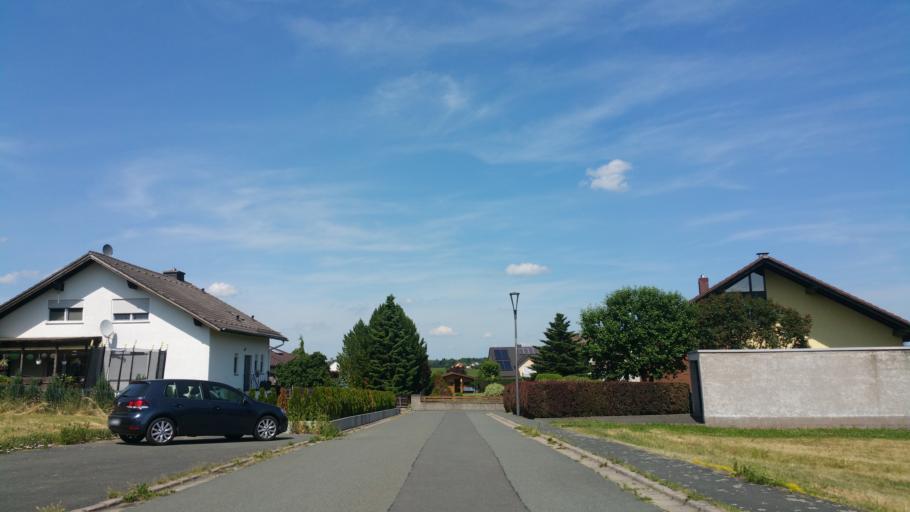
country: DE
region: Bavaria
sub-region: Upper Franconia
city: Schwarzenbach an der Saale
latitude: 50.2123
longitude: 11.9096
